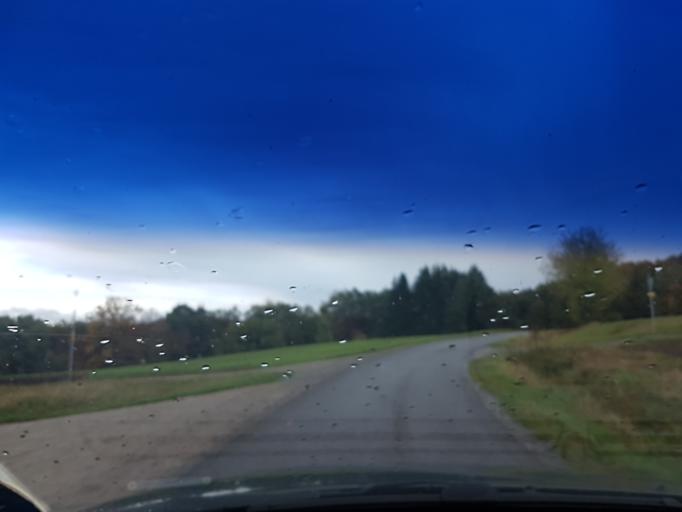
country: DE
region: Bavaria
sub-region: Regierungsbezirk Mittelfranken
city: Markt Taschendorf
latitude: 49.7576
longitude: 10.5306
